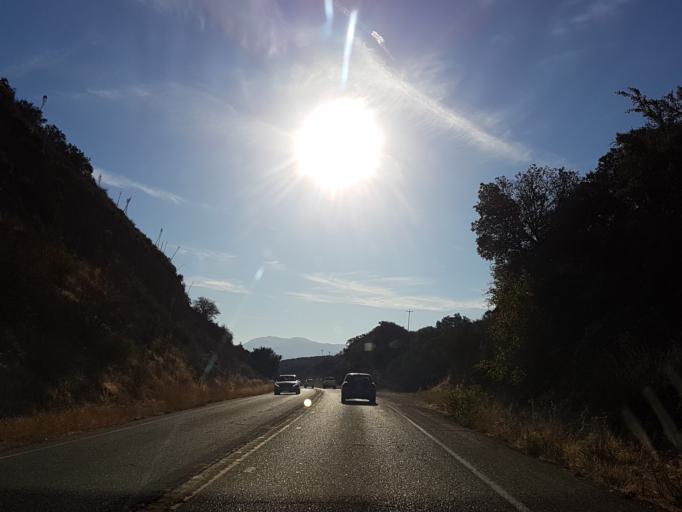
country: US
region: California
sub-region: Santa Barbara County
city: Santa Ynez
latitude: 34.5643
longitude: -119.9360
